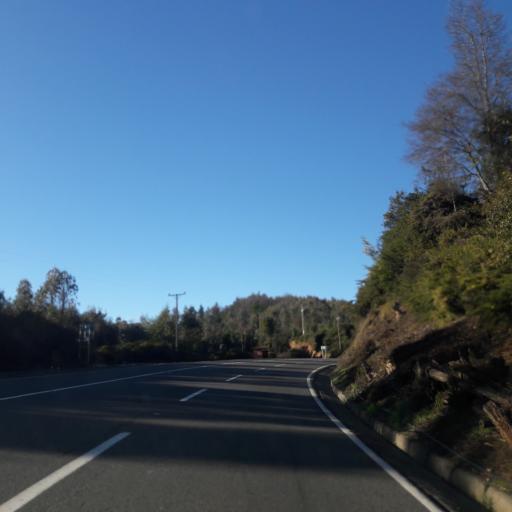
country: CL
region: Biobio
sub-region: Provincia de Biobio
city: La Laja
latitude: -37.2695
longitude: -72.9596
